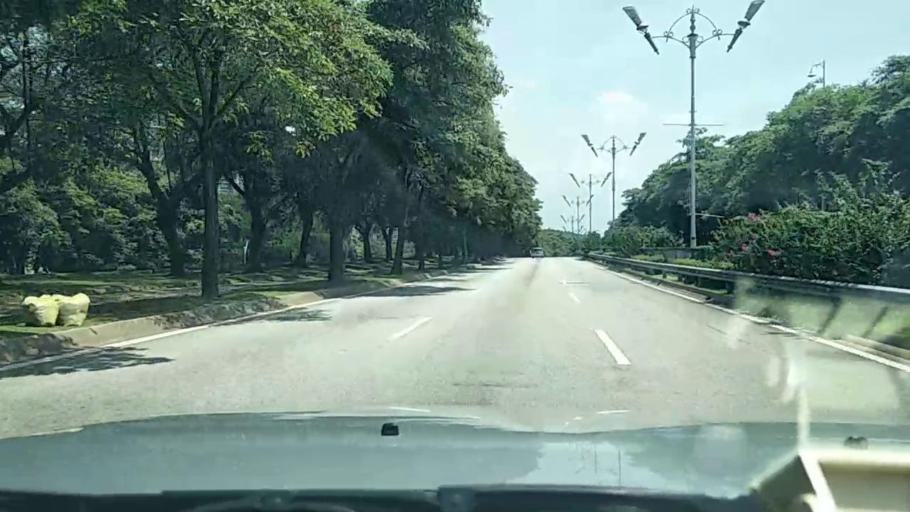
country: MY
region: Putrajaya
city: Putrajaya
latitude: 2.9469
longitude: 101.6787
